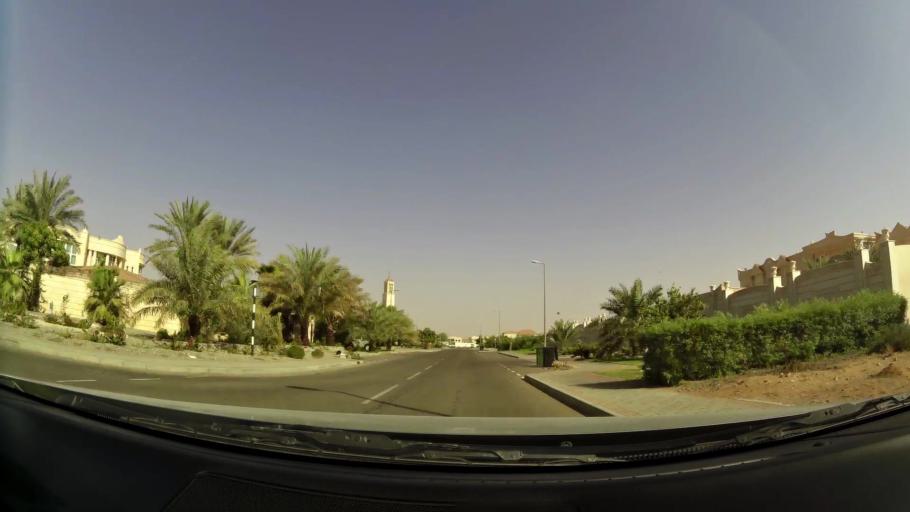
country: OM
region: Al Buraimi
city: Al Buraymi
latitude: 24.3488
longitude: 55.7899
